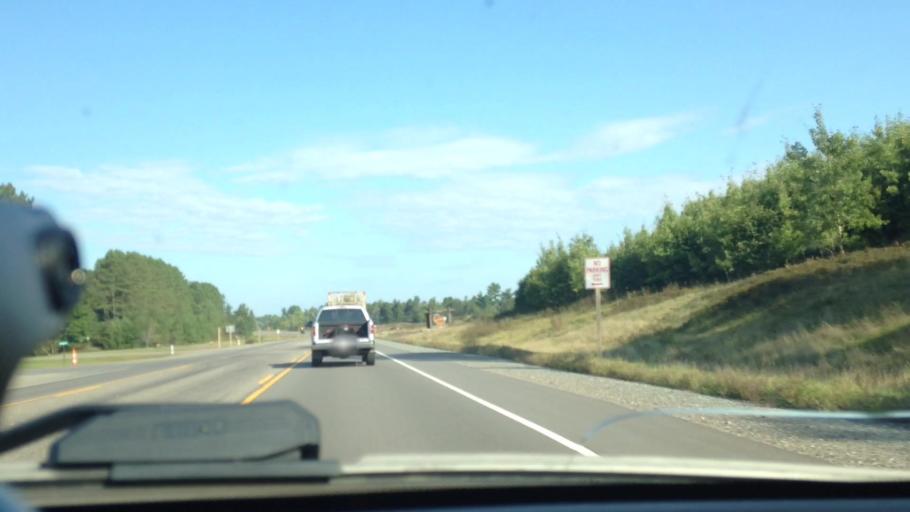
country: US
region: Michigan
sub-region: Dickinson County
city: Iron Mountain
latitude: 45.8703
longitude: -88.0828
